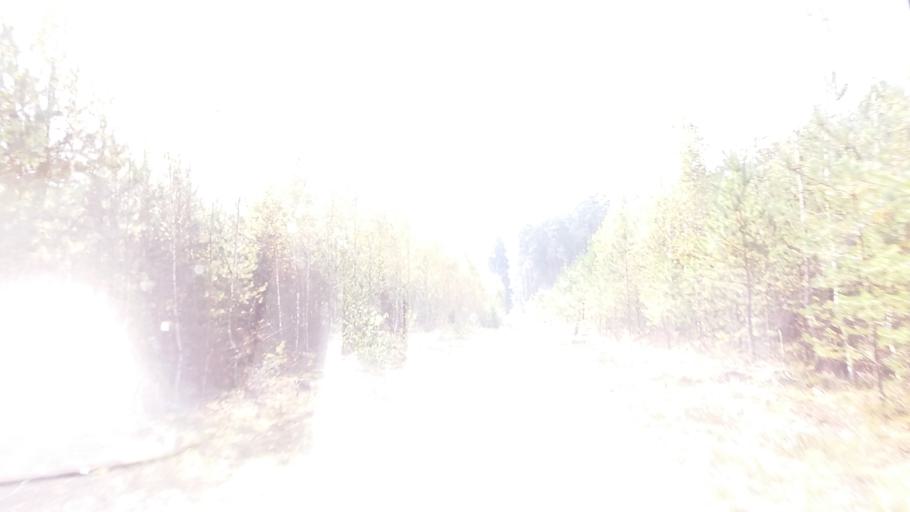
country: PL
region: West Pomeranian Voivodeship
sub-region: Powiat drawski
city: Kalisz Pomorski
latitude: 53.2095
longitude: 15.8965
